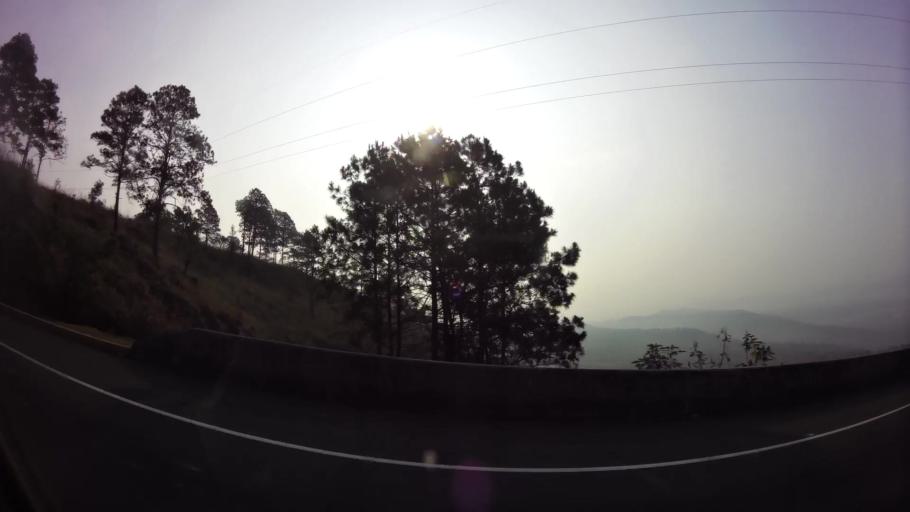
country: HN
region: Francisco Morazan
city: Zambrano
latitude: 14.2497
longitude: -87.3757
